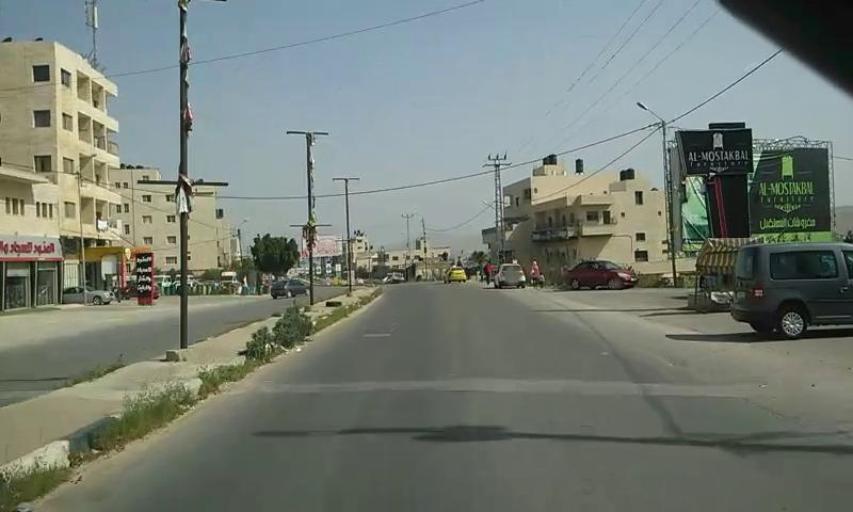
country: PS
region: West Bank
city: Kafr Qallil
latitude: 32.1908
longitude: 35.2833
